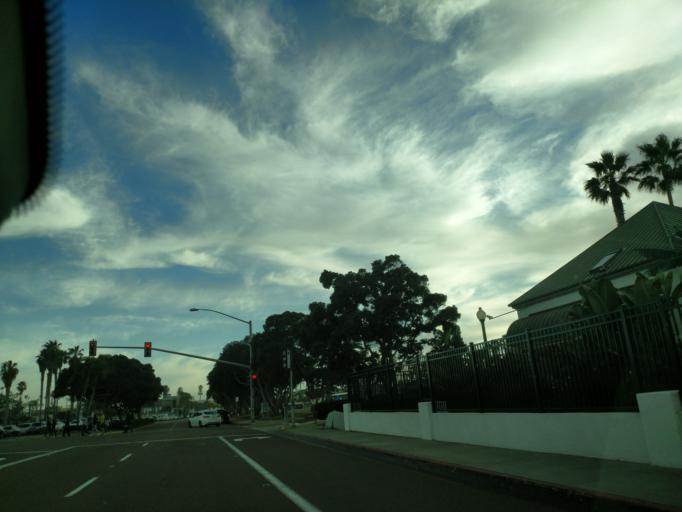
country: US
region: California
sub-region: San Diego County
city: La Jolla
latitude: 32.7702
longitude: -117.2511
